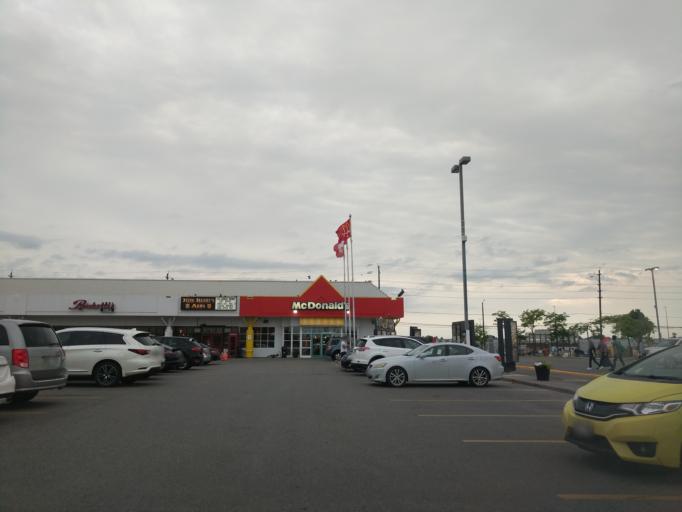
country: CA
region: Ontario
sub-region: York
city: Richmond Hill
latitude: 43.8544
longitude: -79.4318
